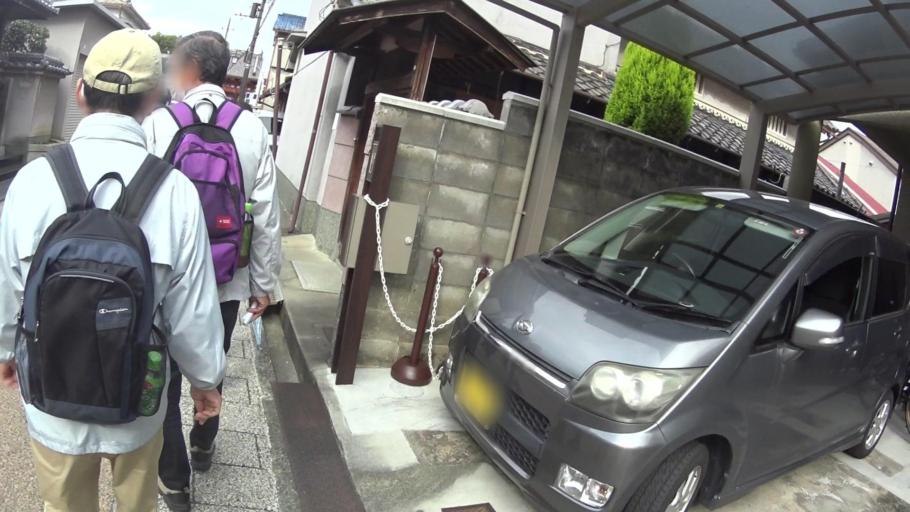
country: JP
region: Osaka
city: Kashihara
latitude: 34.5685
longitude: 135.5967
